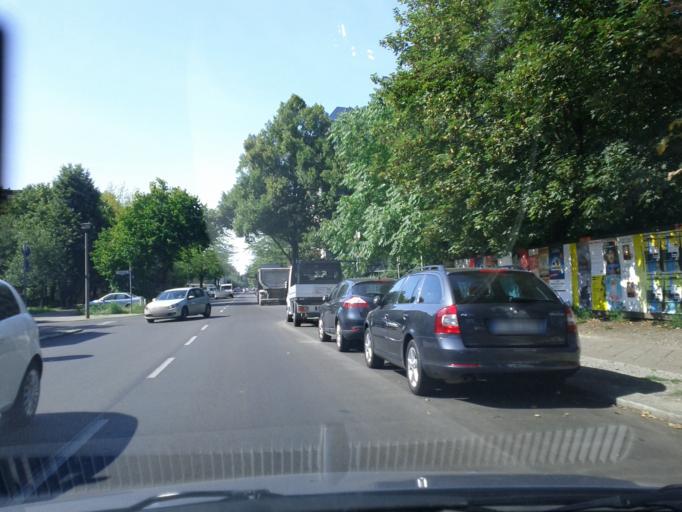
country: DE
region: Berlin
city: Prenzlauer Berg Bezirk
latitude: 52.5498
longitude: 13.4414
